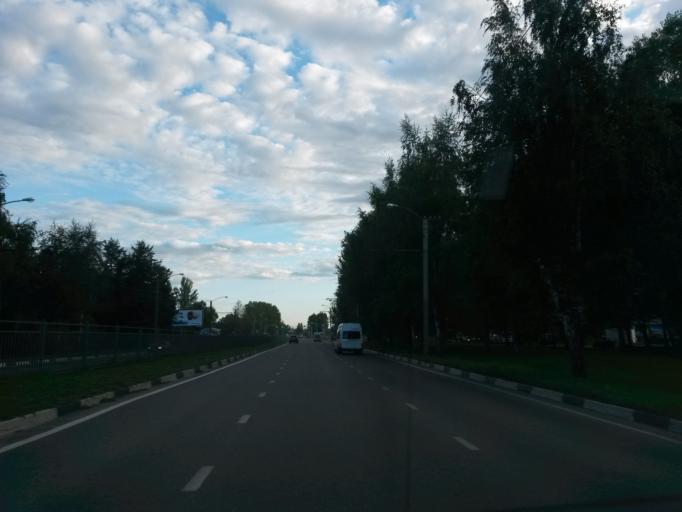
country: RU
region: Jaroslavl
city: Yaroslavl
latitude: 57.6767
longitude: 39.7757
